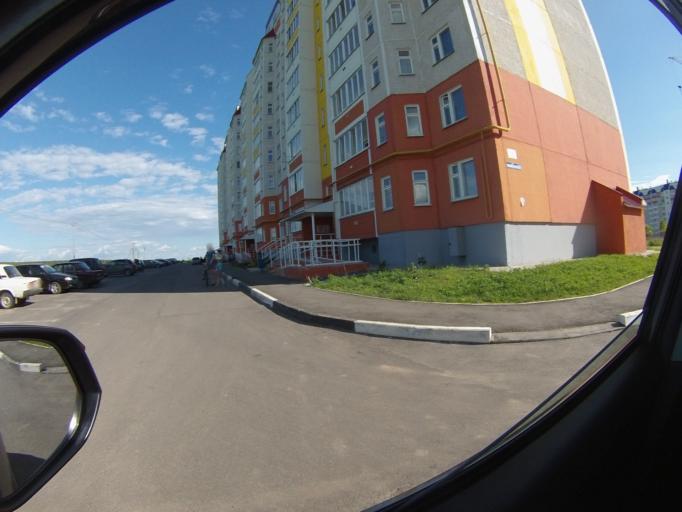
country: RU
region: Orjol
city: Mtsensk
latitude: 53.2935
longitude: 36.6077
